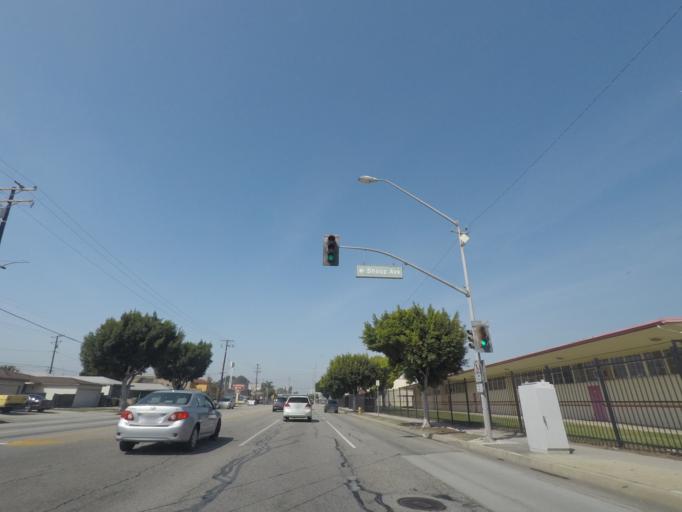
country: US
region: California
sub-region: Los Angeles County
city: Del Aire
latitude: 33.9165
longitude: -118.3642
